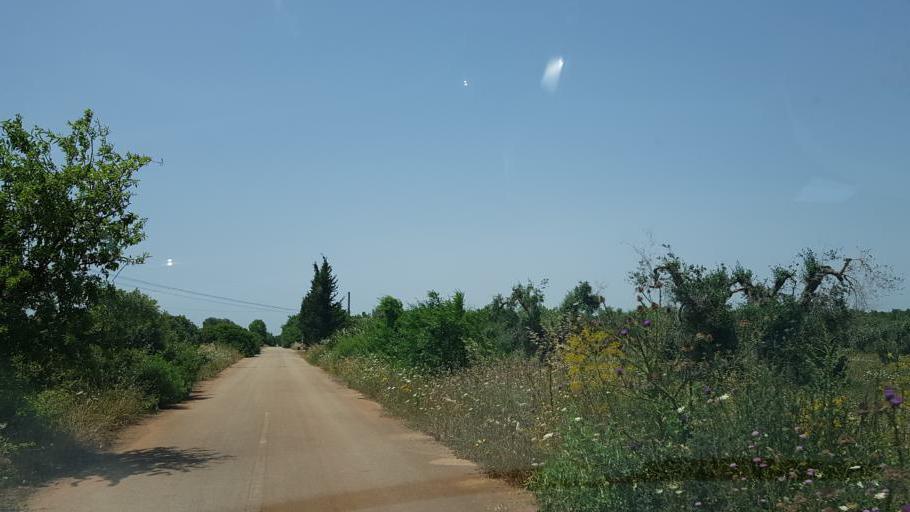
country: IT
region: Apulia
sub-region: Provincia di Lecce
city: Porto Cesareo
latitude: 40.3247
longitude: 17.8765
